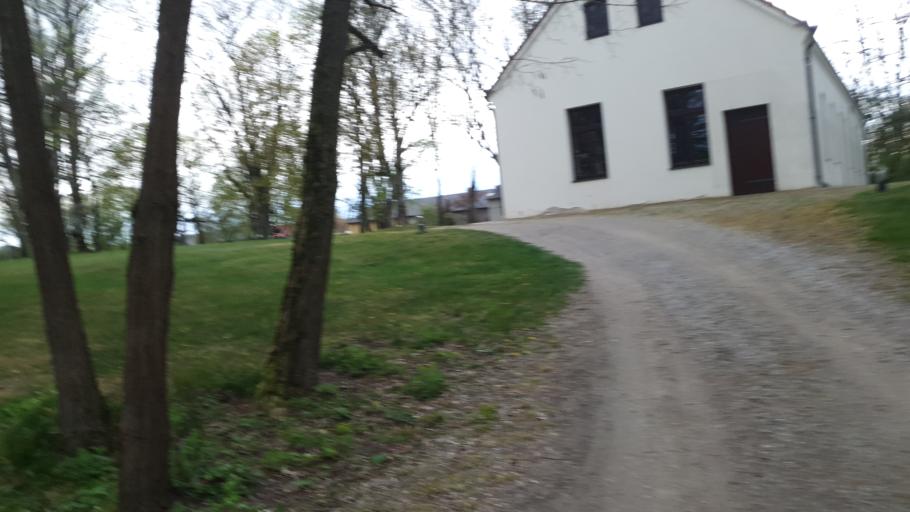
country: LT
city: Gelgaudiskis
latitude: 55.0784
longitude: 22.9792
